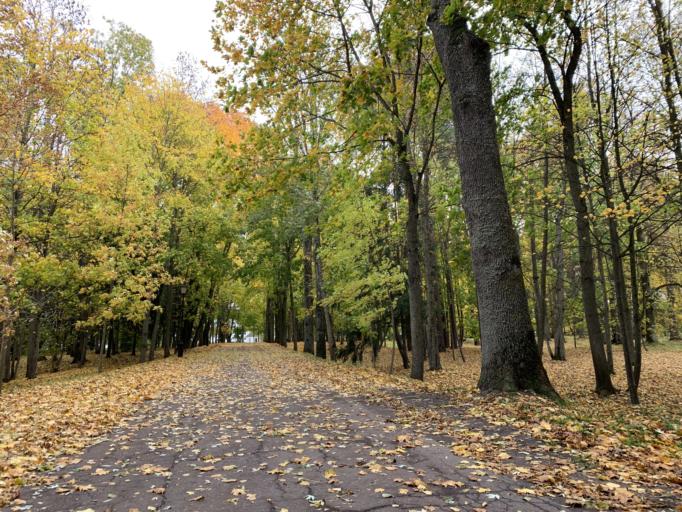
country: BY
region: Minsk
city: Nyasvizh
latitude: 53.2221
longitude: 26.6988
